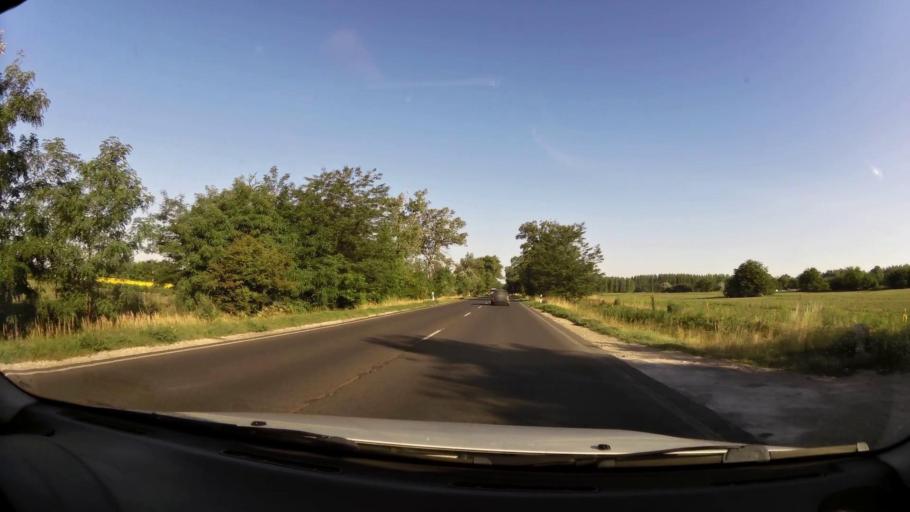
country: HU
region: Pest
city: Pilis
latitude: 47.2950
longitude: 19.5291
